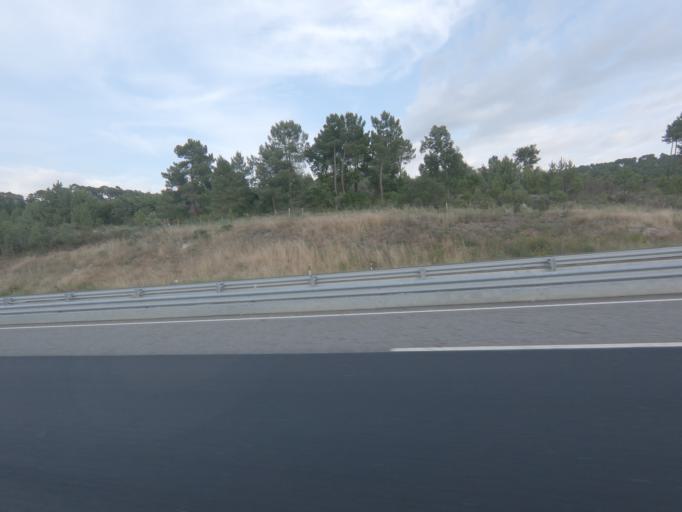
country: PT
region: Vila Real
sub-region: Boticas
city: Boticas
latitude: 41.6205
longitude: -7.6038
